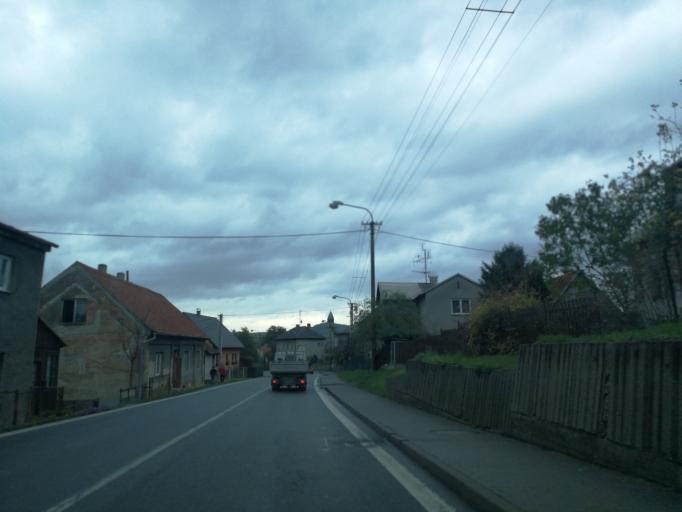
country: CZ
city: Hodslavice
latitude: 49.5335
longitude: 18.0196
